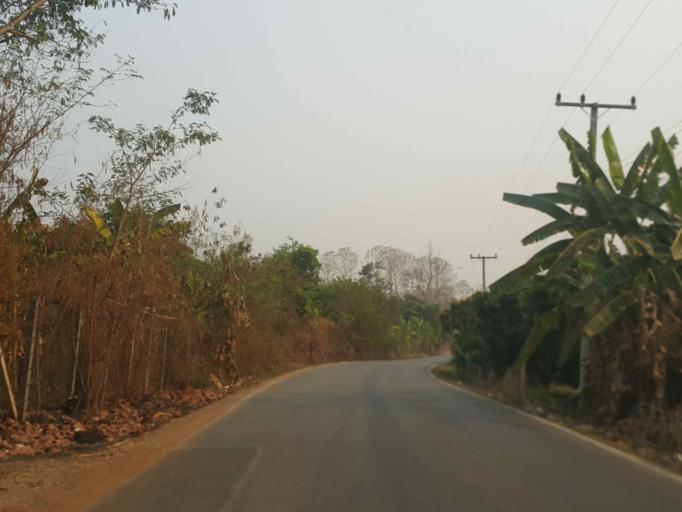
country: TH
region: Chiang Mai
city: Mae Taeng
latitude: 19.0971
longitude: 98.9010
